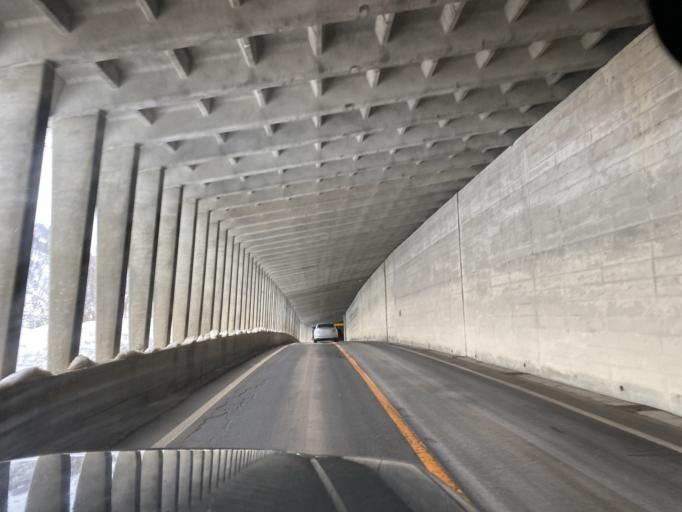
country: JP
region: Gifu
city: Takayama
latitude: 36.1019
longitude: 136.9285
